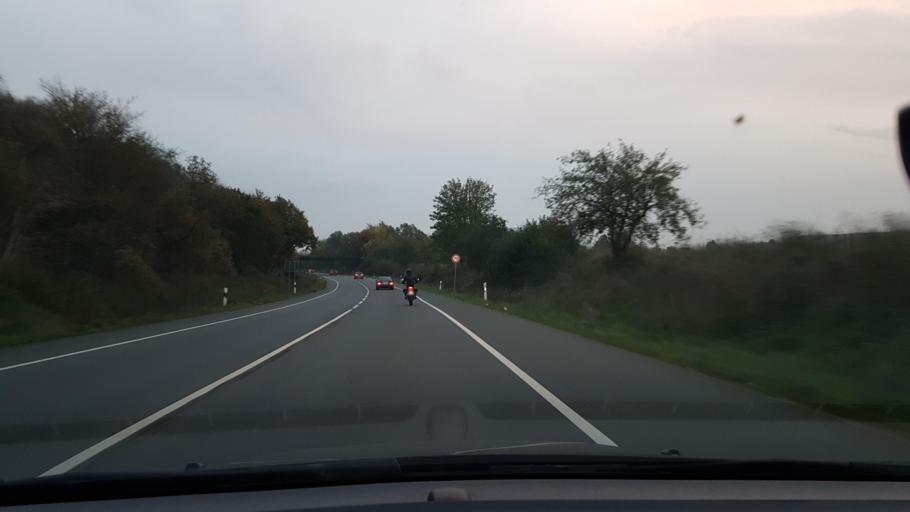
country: DE
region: Lower Saxony
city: Wunstorf
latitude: 52.4257
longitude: 9.4603
